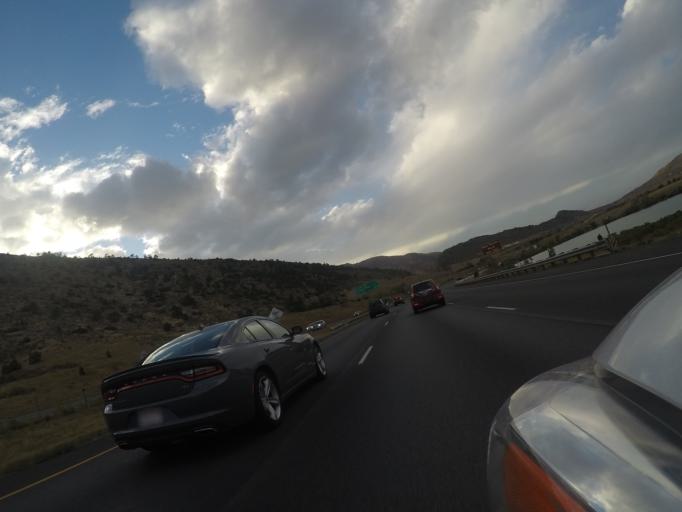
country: US
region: Colorado
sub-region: Jefferson County
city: Indian Hills
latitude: 39.6441
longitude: -105.1775
